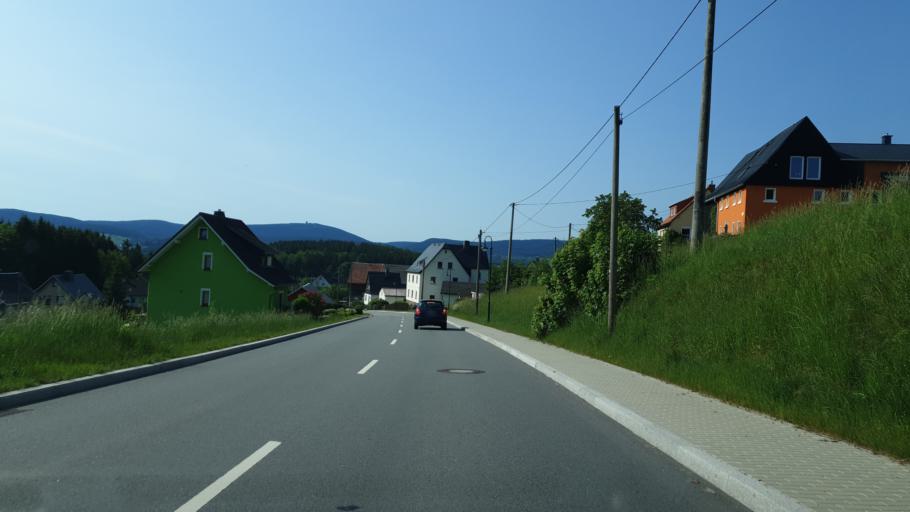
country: DE
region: Saxony
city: Zschorlau
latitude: 50.5350
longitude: 12.6205
